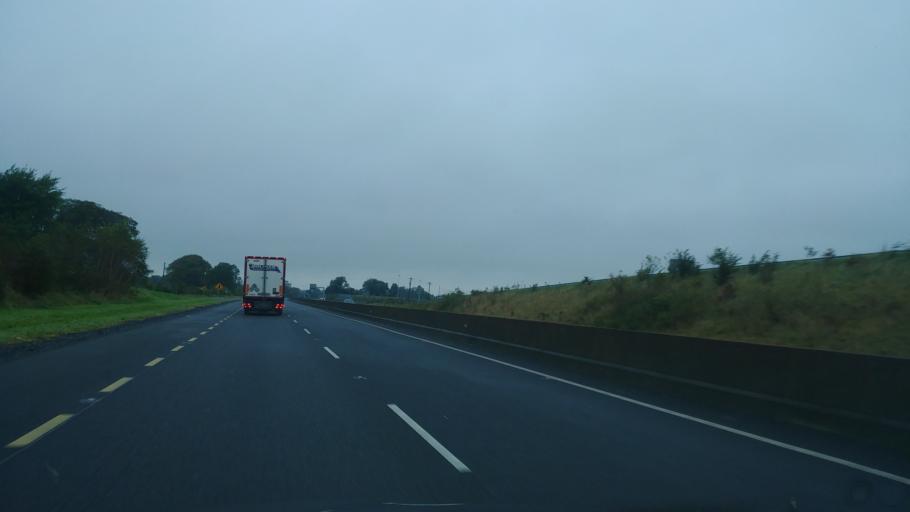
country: IE
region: Leinster
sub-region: An Iarmhi
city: Rathwire
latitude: 53.5013
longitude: -7.2355
